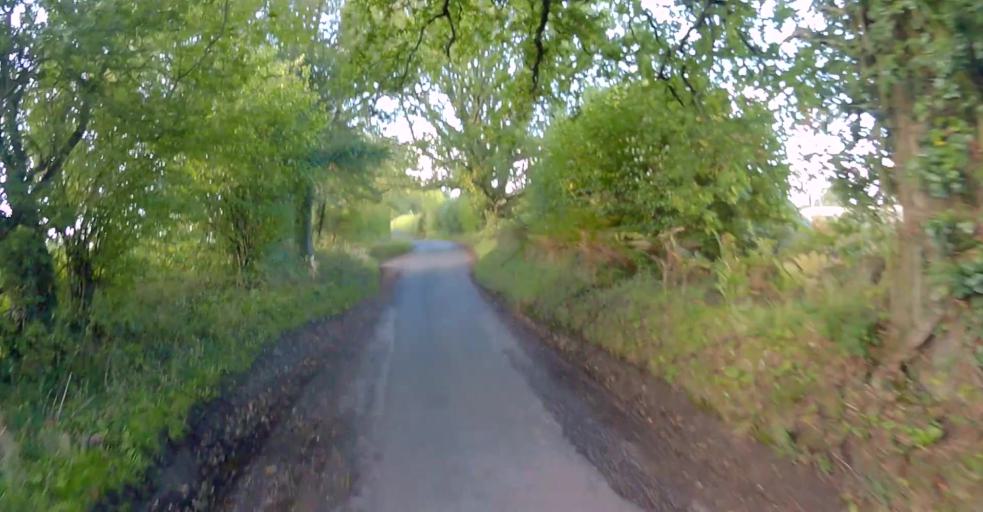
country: GB
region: England
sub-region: Hampshire
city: Long Sutton
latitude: 51.2106
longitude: -0.9059
